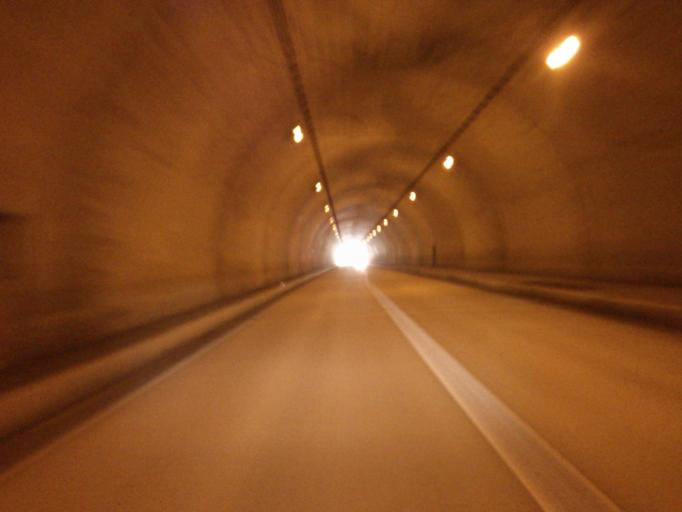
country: JP
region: Kyoto
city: Fukuchiyama
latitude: 35.2969
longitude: 135.0105
